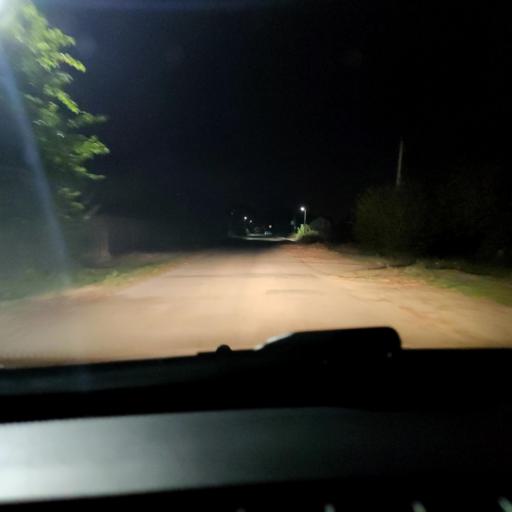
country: RU
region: Voronezj
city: Shilovo
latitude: 51.5321
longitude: 39.0467
